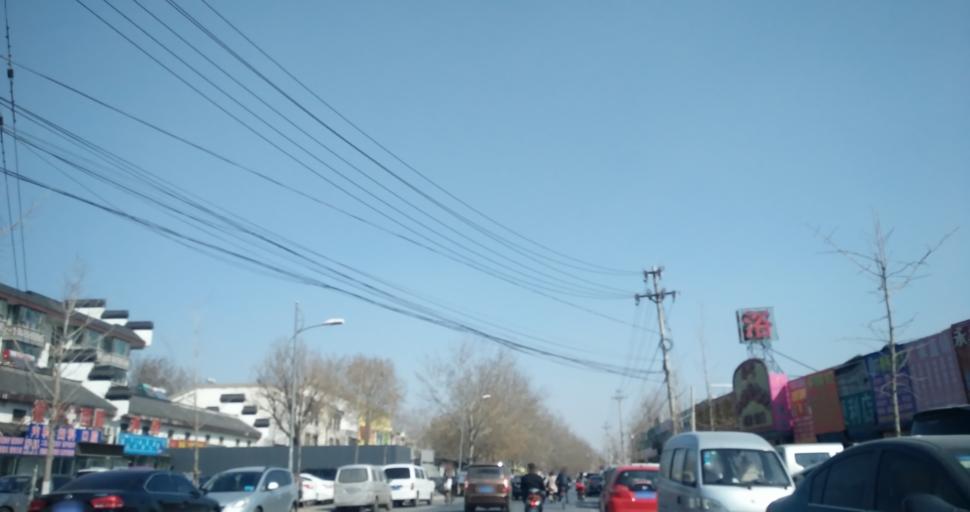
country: CN
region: Beijing
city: Jiugong
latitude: 39.8083
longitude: 116.4442
